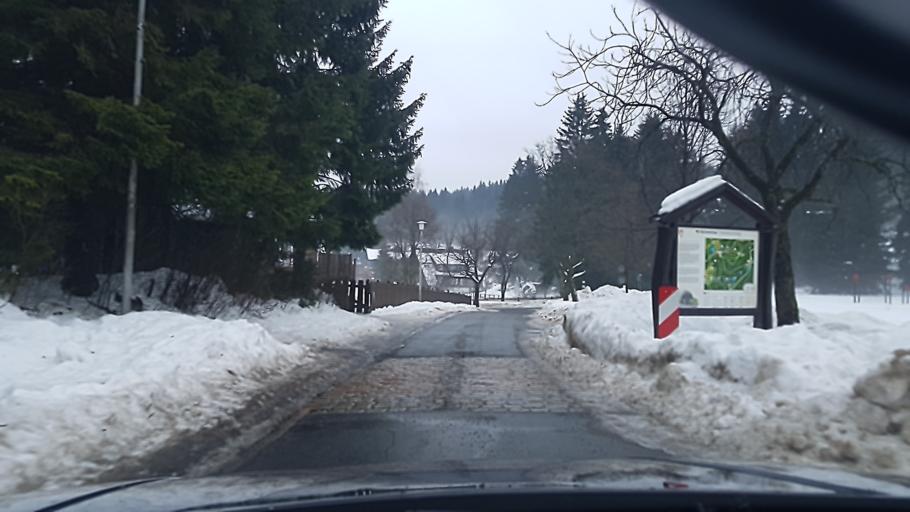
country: DE
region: Lower Saxony
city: Clausthal-Zellerfeld
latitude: 51.8484
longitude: 10.3313
